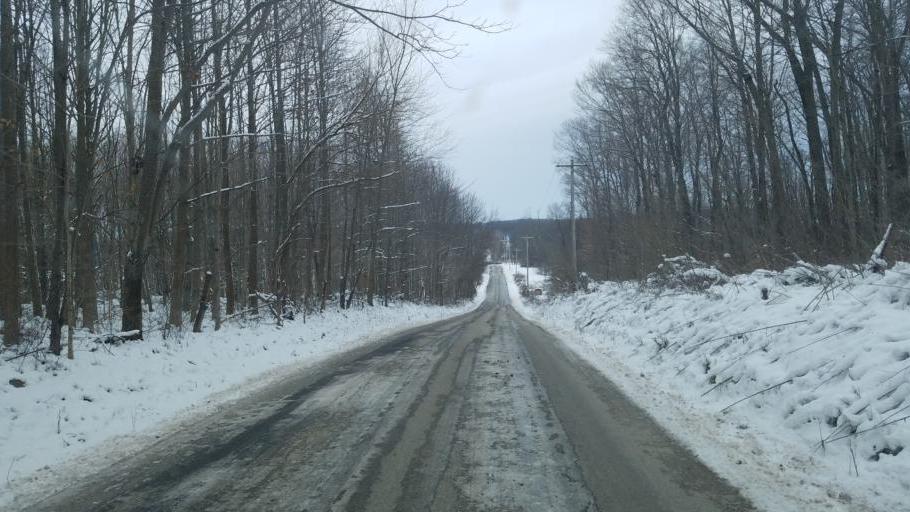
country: US
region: Ohio
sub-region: Knox County
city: Fredericktown
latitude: 40.5364
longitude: -82.6333
